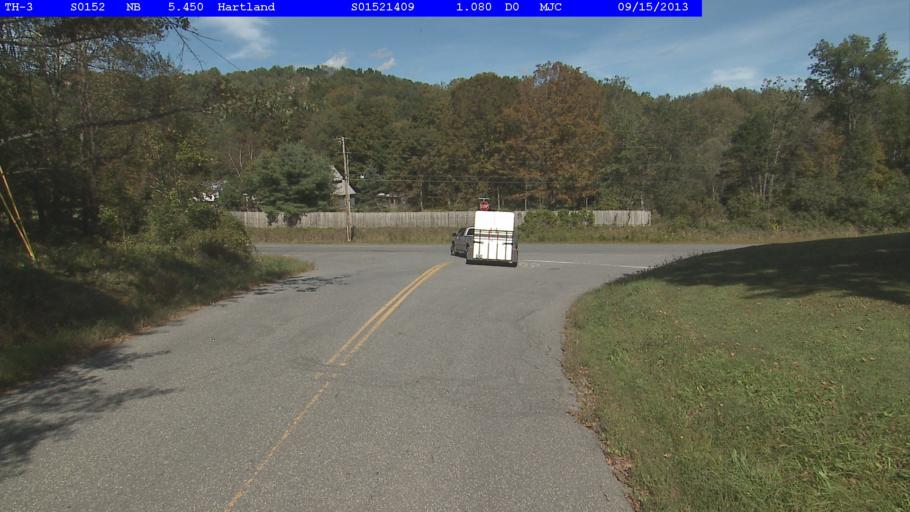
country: US
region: Vermont
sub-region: Windsor County
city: Windsor
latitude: 43.5366
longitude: -72.4335
